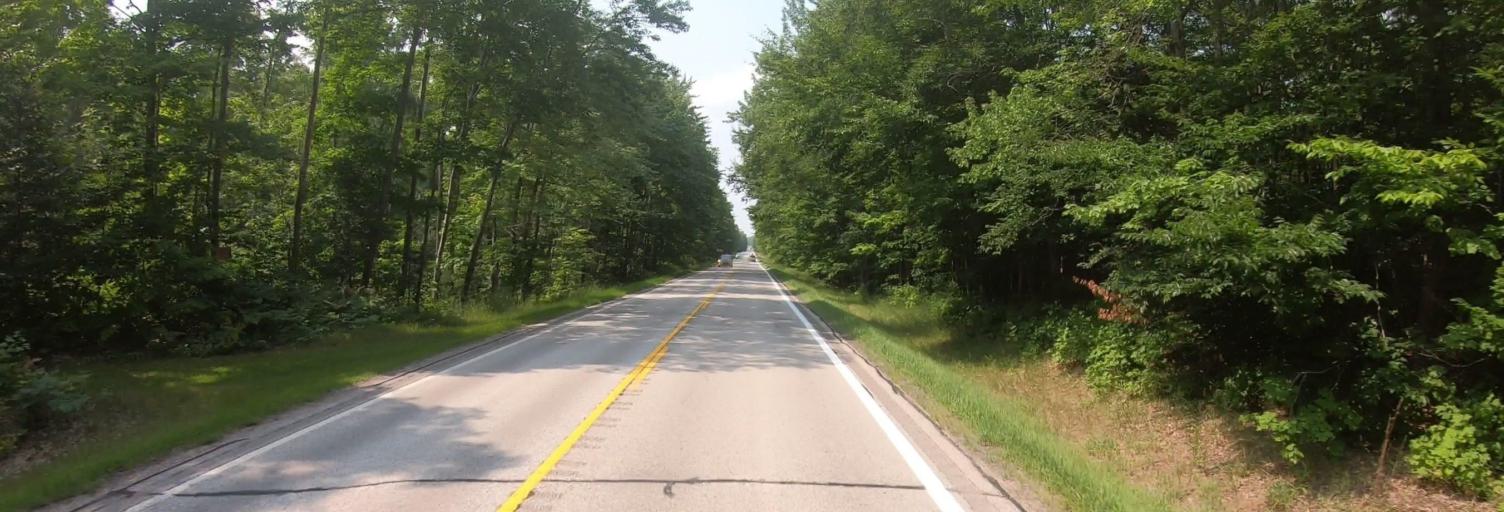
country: US
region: Michigan
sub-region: Luce County
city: Newberry
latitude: 46.5251
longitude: -85.4092
